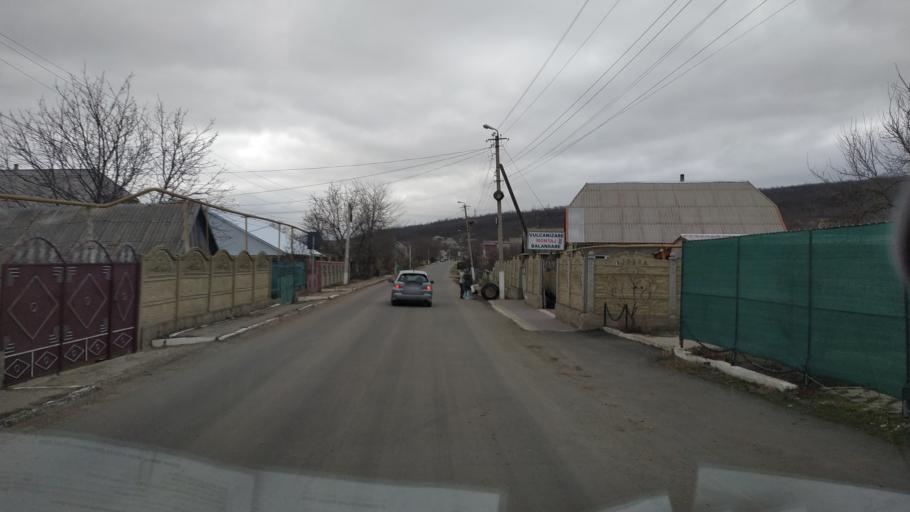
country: MD
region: Causeni
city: Causeni
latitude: 46.6497
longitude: 29.4406
